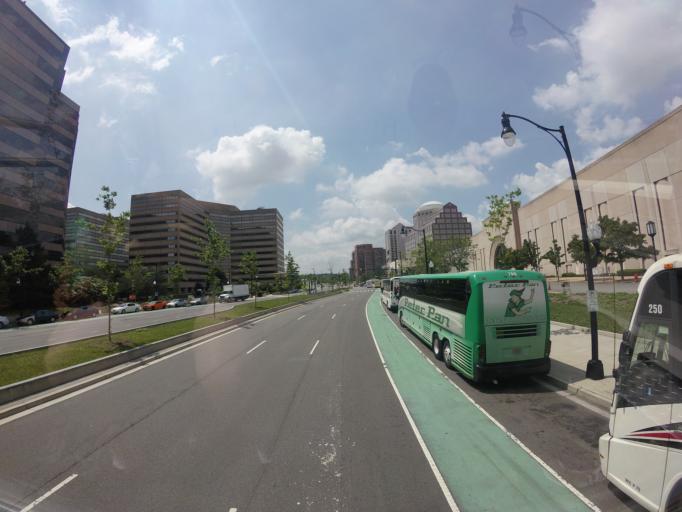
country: US
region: Washington, D.C.
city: Washington, D.C.
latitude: 38.8649
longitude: -77.0588
